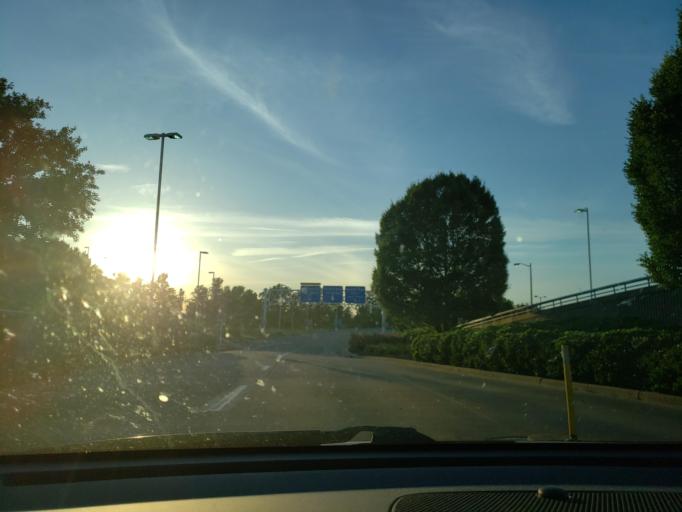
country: US
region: Virginia
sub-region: Henrico County
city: Fort Lee
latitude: 37.5105
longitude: -77.3329
